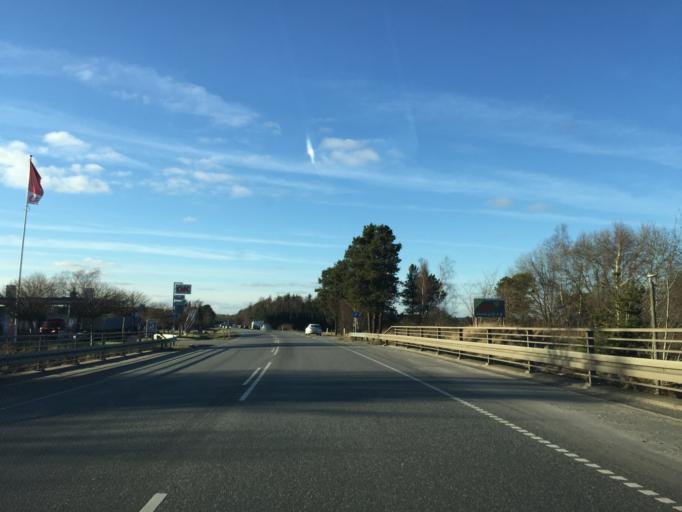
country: DK
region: Central Jutland
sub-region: Viborg Kommune
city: Bjerringbro
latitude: 56.2707
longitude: 9.7301
